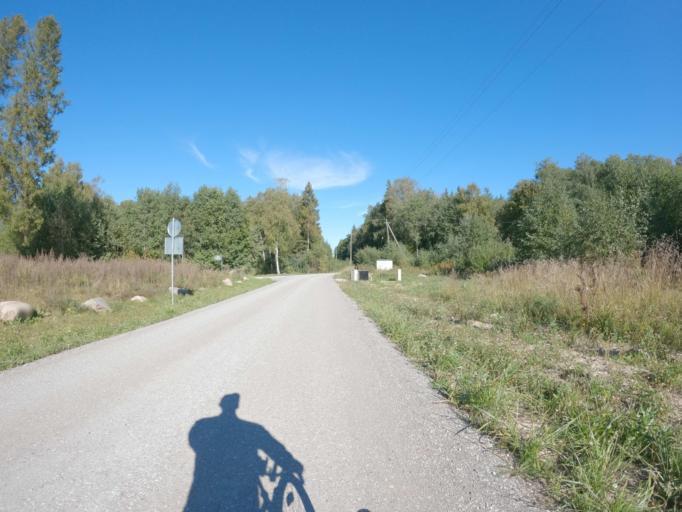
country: EE
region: Raplamaa
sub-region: Rapla vald
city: Rapla
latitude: 58.9906
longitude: 24.8108
